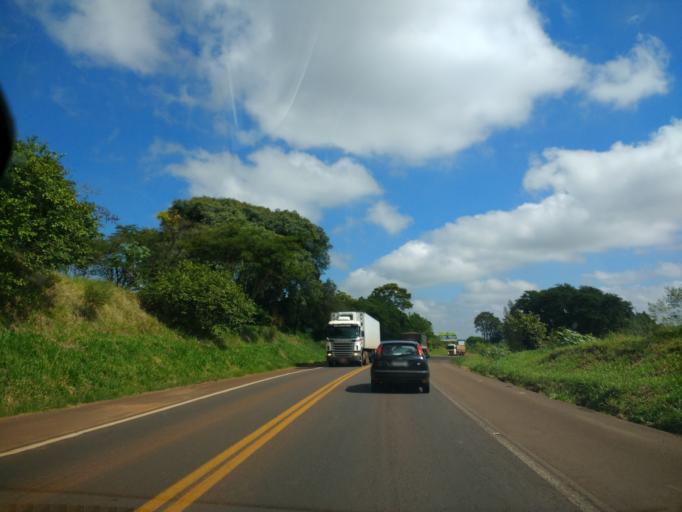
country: BR
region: Parana
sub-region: Cruzeiro Do Oeste
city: Cruzeiro do Oeste
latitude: -23.7716
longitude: -53.1650
